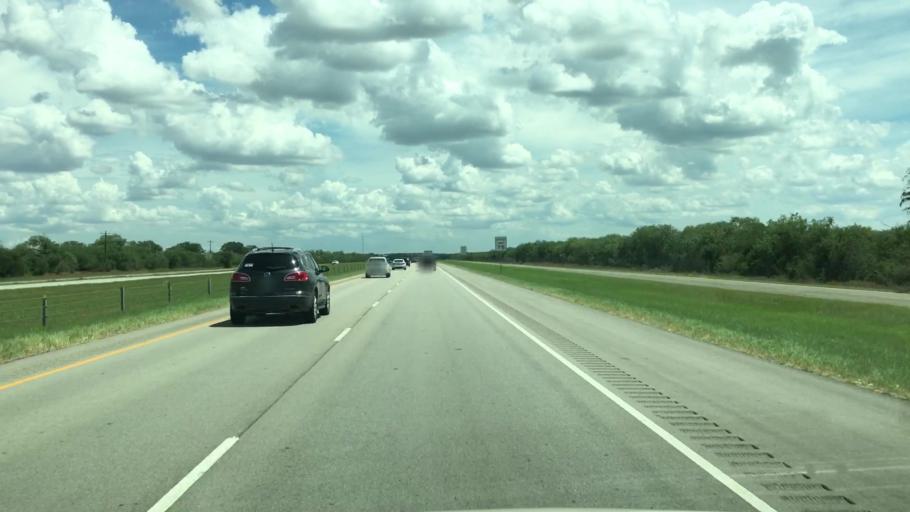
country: US
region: Texas
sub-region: Live Oak County
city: George West
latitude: 28.2812
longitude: -97.9567
